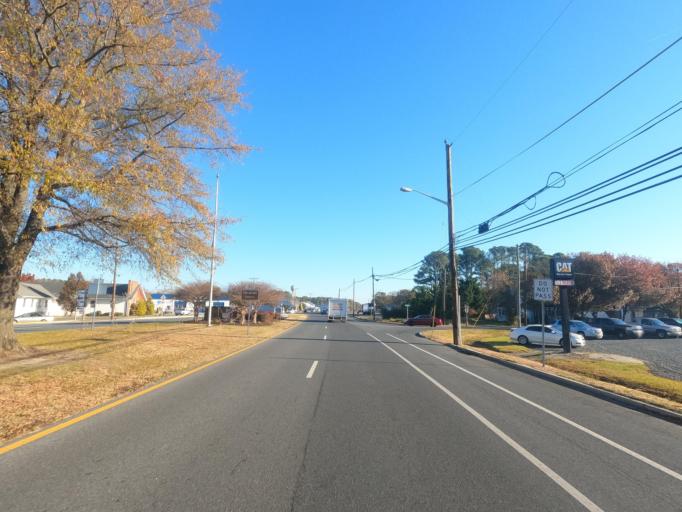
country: US
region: Maryland
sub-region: Somerset County
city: Crisfield
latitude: 37.9917
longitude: -75.8428
